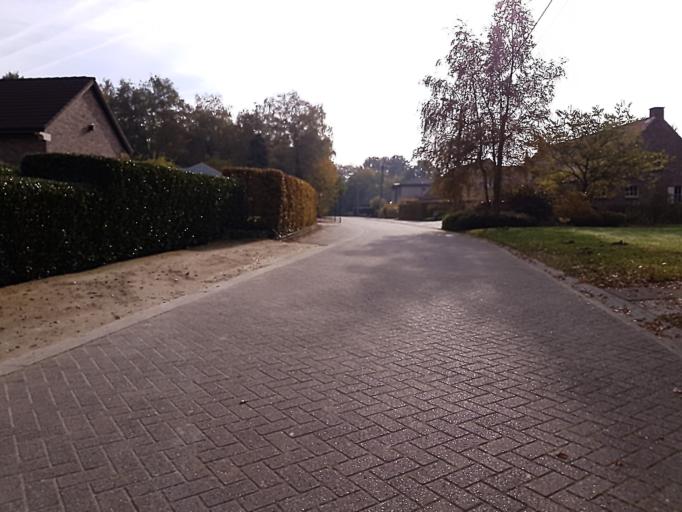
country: BE
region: Flanders
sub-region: Provincie Antwerpen
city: Sint-Katelijne-Waver
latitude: 51.0591
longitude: 4.5099
